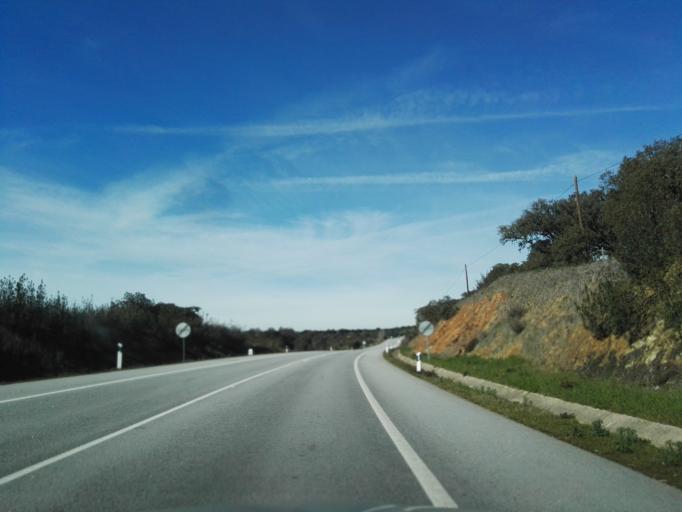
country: PT
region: Portalegre
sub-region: Portalegre
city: Urra
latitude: 39.1914
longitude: -7.3582
